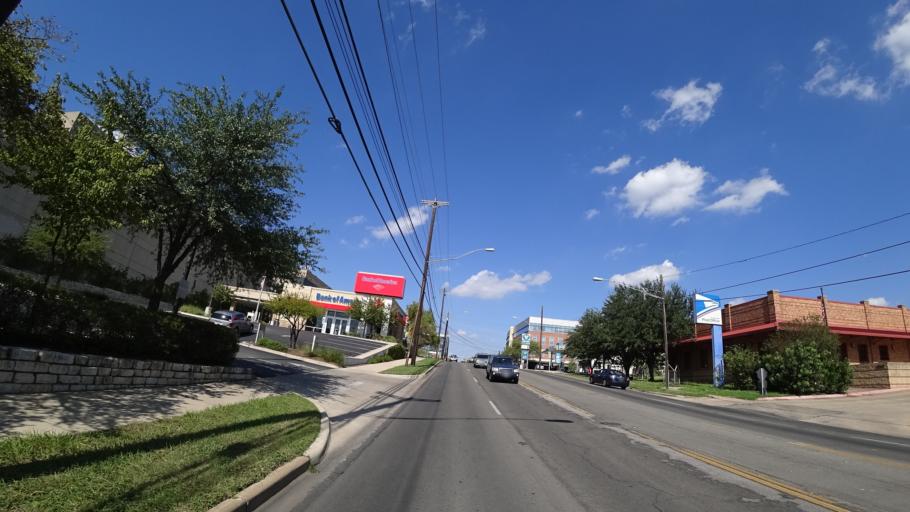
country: US
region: Texas
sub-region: Travis County
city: Austin
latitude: 30.3036
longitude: -97.7442
